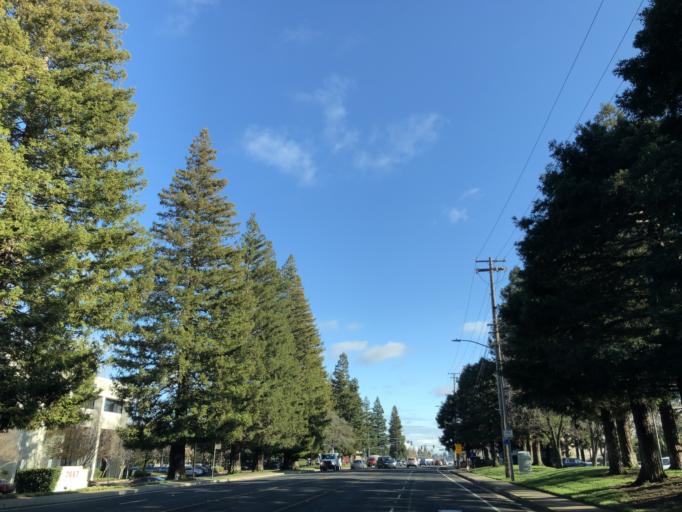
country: US
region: California
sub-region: Sacramento County
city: Rosemont
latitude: 38.5506
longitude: -121.4150
